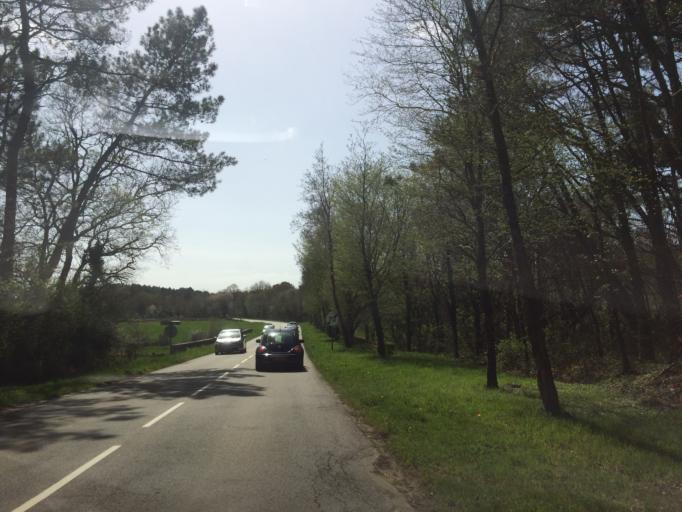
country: FR
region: Brittany
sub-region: Departement du Morbihan
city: Ploemel
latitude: 47.6244
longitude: -3.0518
